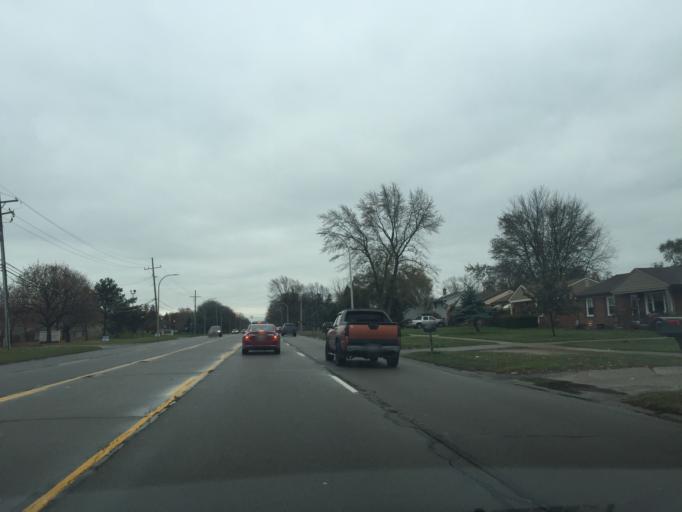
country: US
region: Michigan
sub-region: Wayne County
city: Redford
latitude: 42.4215
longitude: -83.3357
